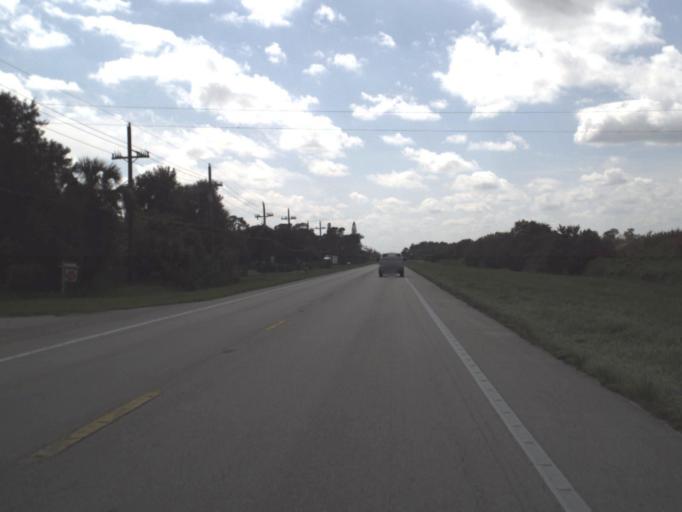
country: US
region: Florida
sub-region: Hendry County
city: LaBelle
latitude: 26.6829
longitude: -81.4367
